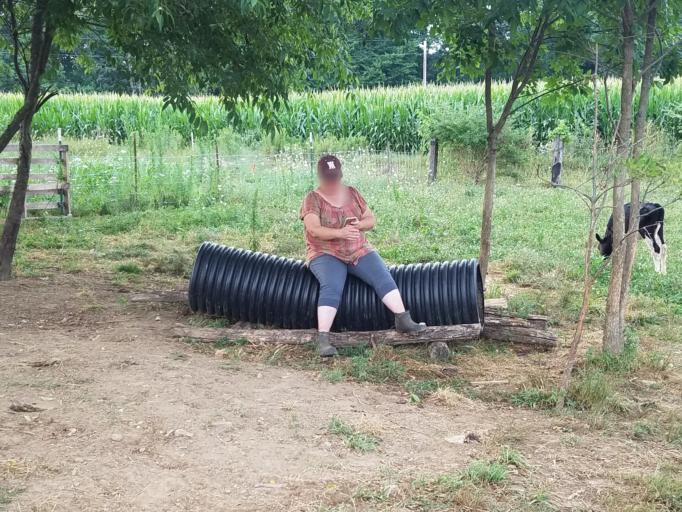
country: US
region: Ohio
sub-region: Knox County
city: Oak Hill
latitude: 40.3132
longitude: -82.2100
